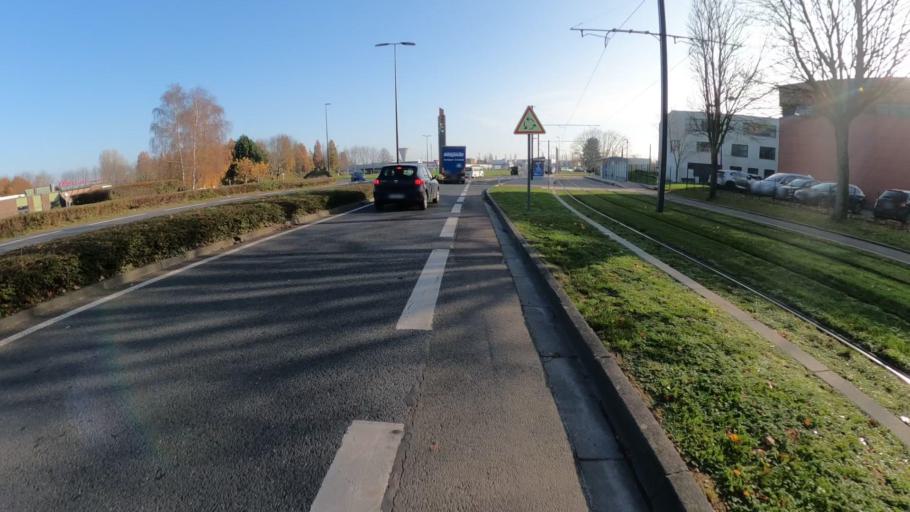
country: FR
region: Lower Normandy
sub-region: Departement du Calvados
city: Epron
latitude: 49.2116
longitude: -0.3573
